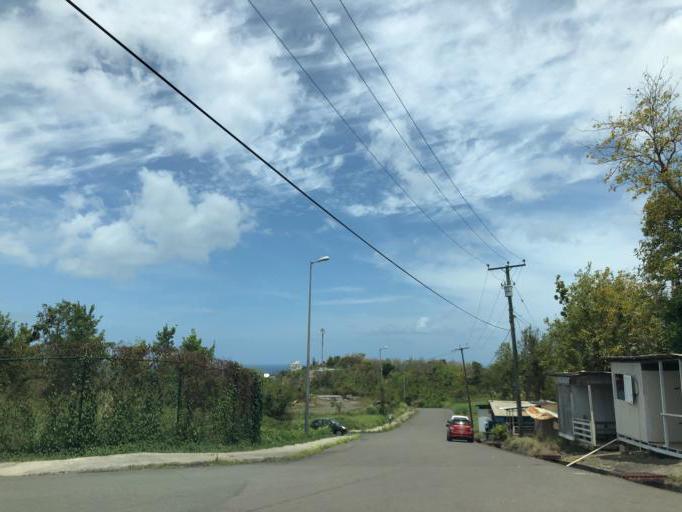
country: LC
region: Castries Quarter
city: Castries
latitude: 14.0023
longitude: -61.0096
